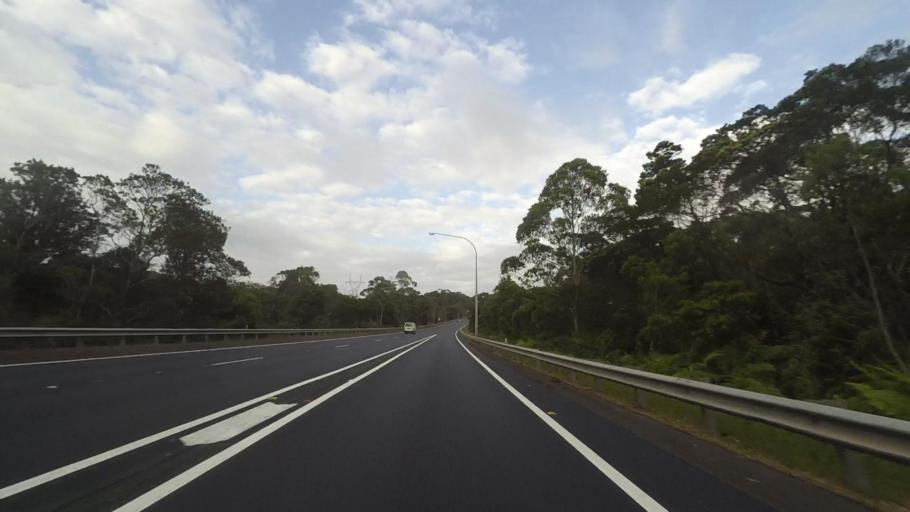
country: AU
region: New South Wales
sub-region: Wollongong
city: Bulli
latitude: -34.3069
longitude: 150.9002
